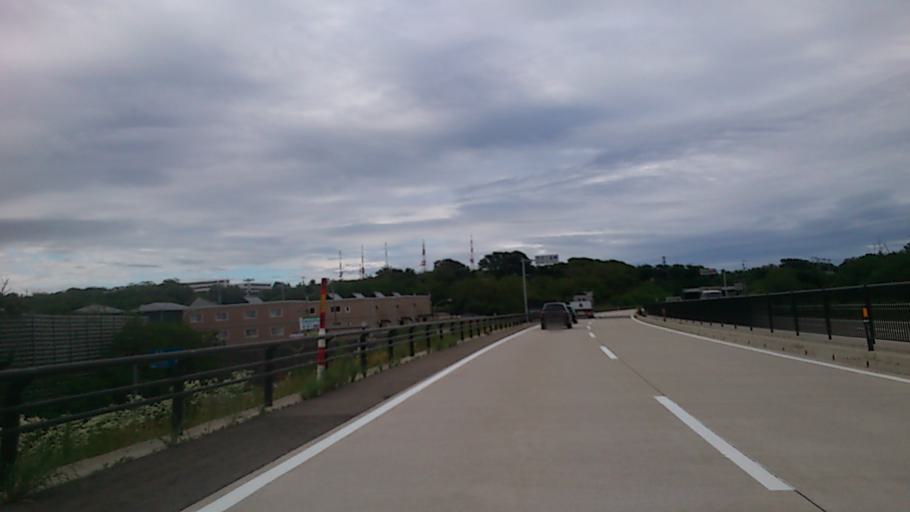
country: JP
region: Akita
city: Akita Shi
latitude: 39.6807
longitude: 140.0736
